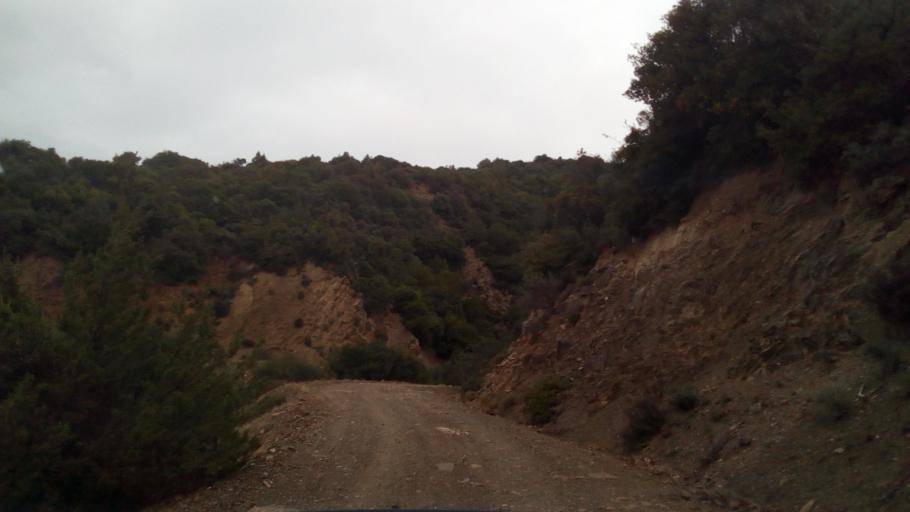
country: GR
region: West Greece
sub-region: Nomos Achaias
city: Temeni
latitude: 38.3701
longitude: 22.1582
